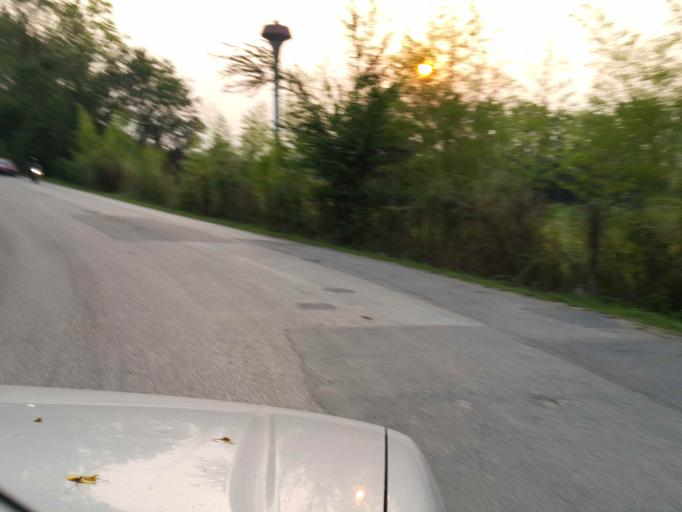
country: TH
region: Chiang Mai
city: San Sai
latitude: 18.9028
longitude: 99.0105
